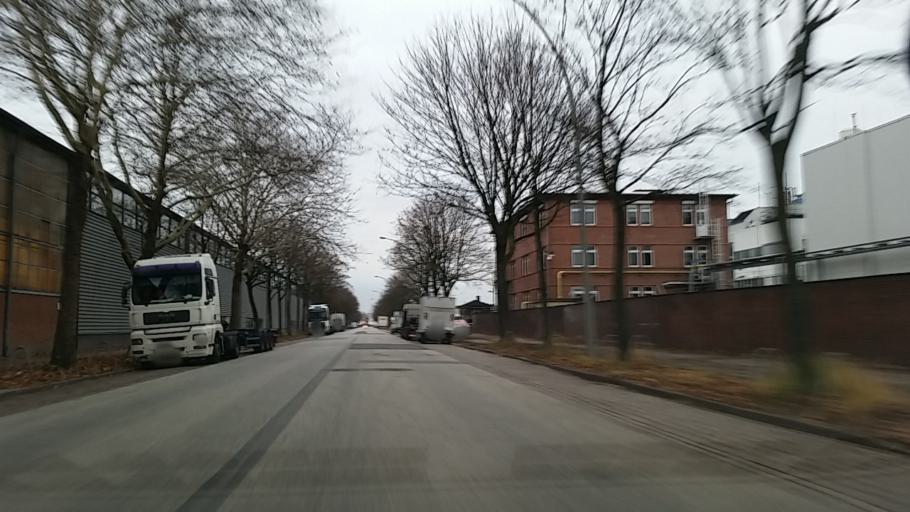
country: DE
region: Hamburg
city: Wandsbek
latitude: 53.5350
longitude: 10.0926
